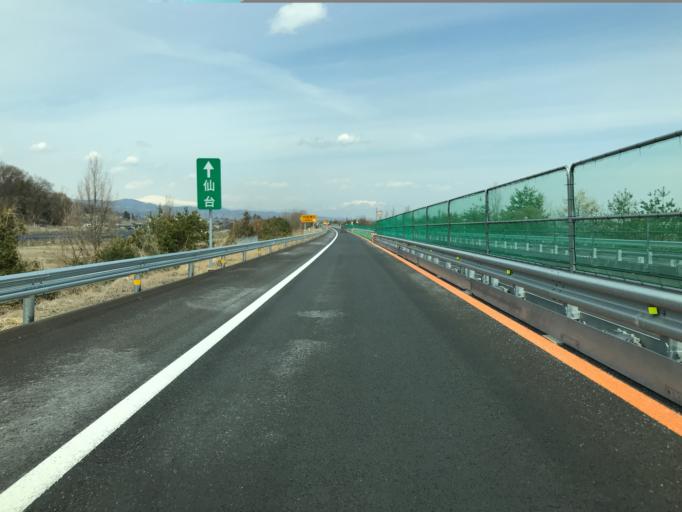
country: JP
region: Yamagata
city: Kaminoyama
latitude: 38.1981
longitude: 140.2976
